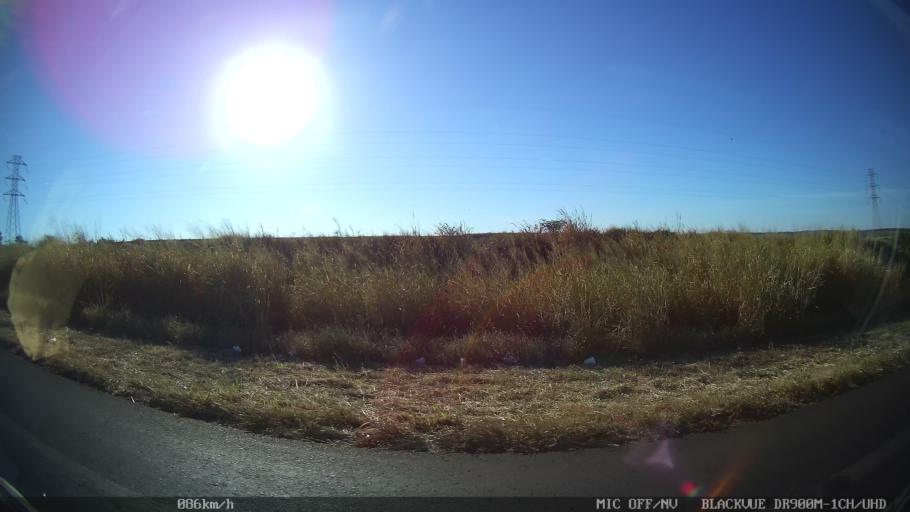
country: BR
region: Sao Paulo
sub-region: Olimpia
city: Olimpia
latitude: -20.6966
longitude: -48.9303
